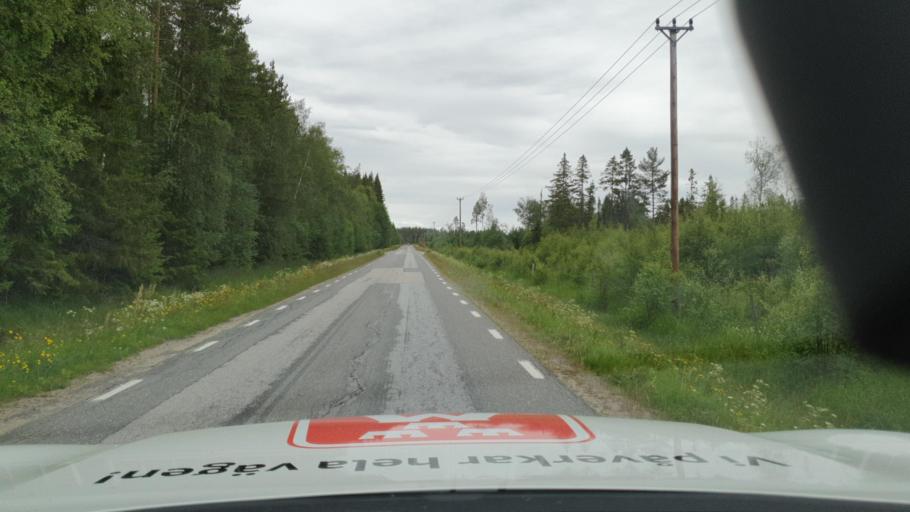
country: SE
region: Vaesterbotten
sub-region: Nordmalings Kommun
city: Nordmaling
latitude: 63.5103
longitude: 19.4211
